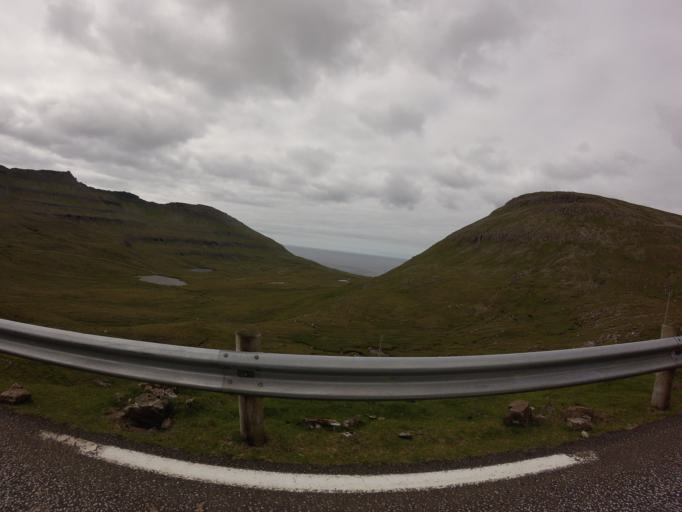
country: FO
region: Suduroy
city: Tvoroyri
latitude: 61.5230
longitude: -6.8373
